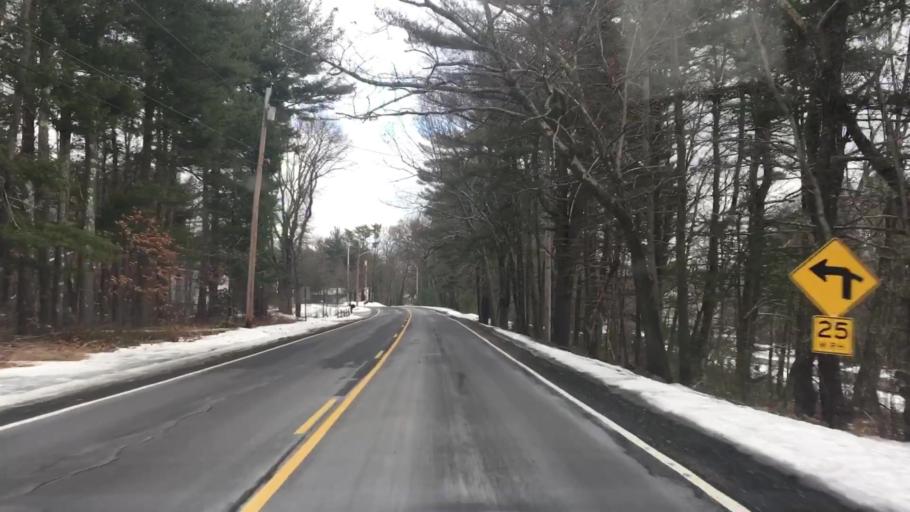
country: US
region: Maine
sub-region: York County
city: Wells Beach Station
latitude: 43.3282
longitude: -70.6267
